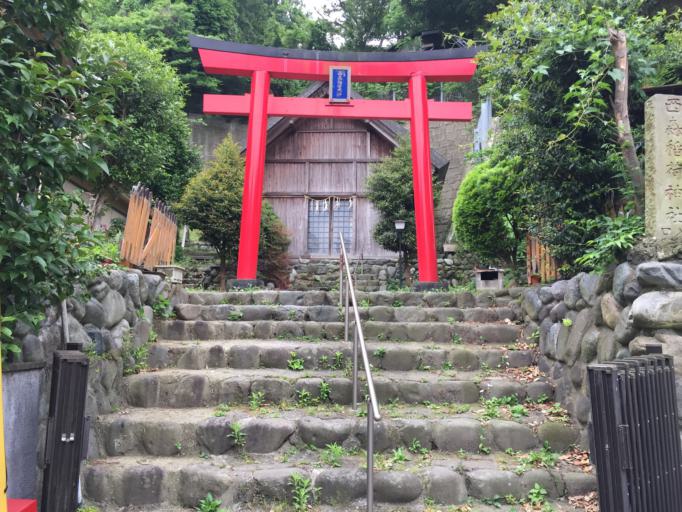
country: JP
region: Kanagawa
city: Yokohama
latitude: 35.4272
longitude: 139.6081
